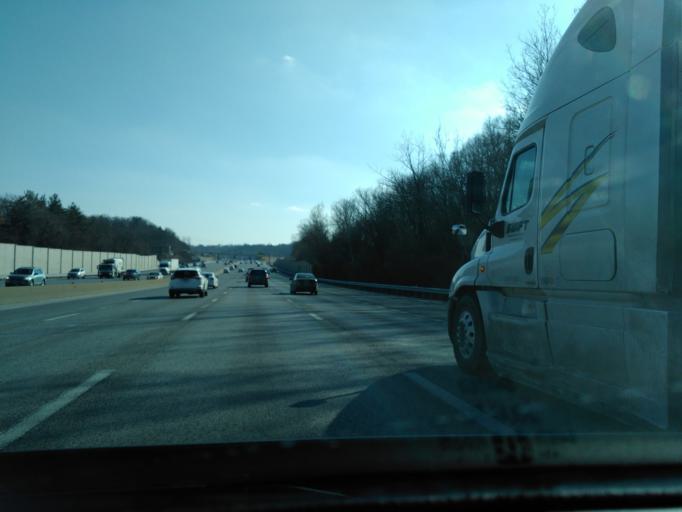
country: US
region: Missouri
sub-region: Saint Louis County
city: Des Peres
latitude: 38.5892
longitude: -90.4491
